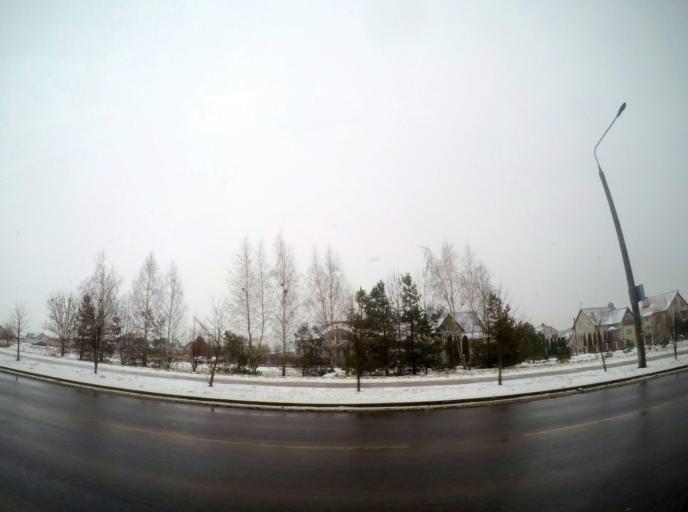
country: BY
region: Grodnenskaya
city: Hrodna
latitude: 53.6203
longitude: 23.8221
